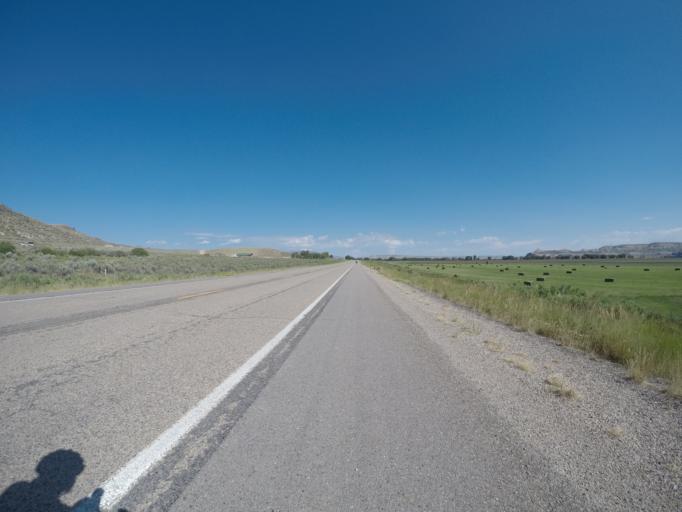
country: US
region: Wyoming
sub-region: Sublette County
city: Marbleton
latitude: 42.2059
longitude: -110.1824
